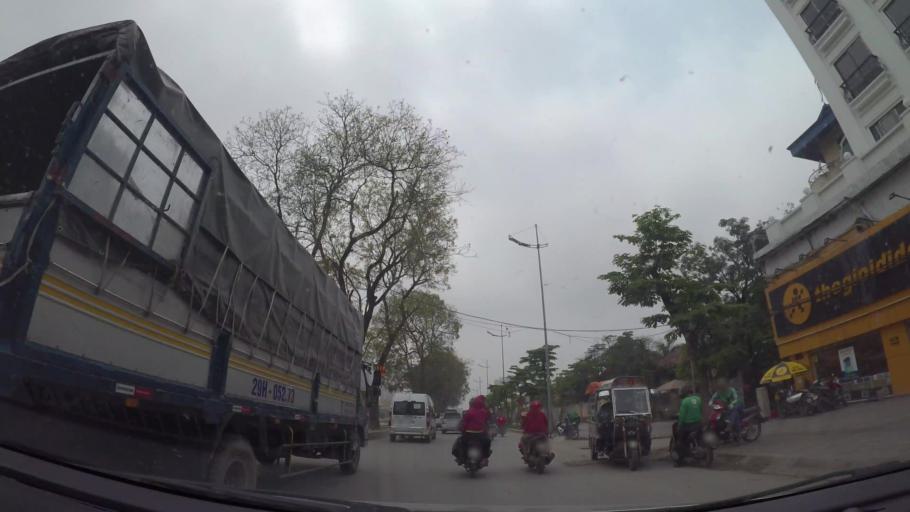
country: VN
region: Ha Noi
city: Cau Dien
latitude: 21.0425
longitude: 105.7808
